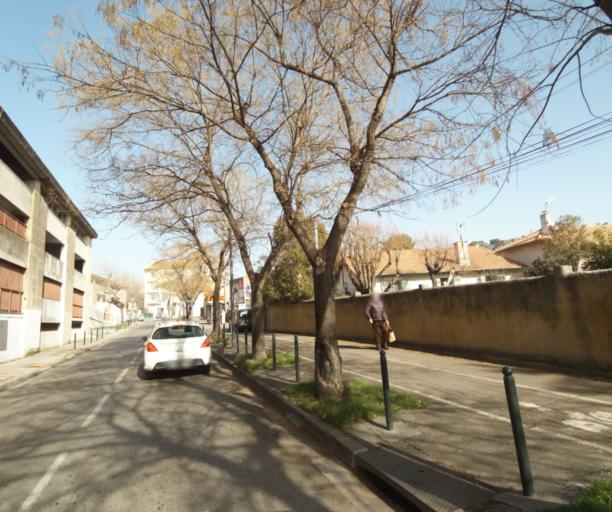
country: FR
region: Provence-Alpes-Cote d'Azur
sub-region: Departement des Bouches-du-Rhone
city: Aix-en-Provence
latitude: 43.5339
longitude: 5.4467
